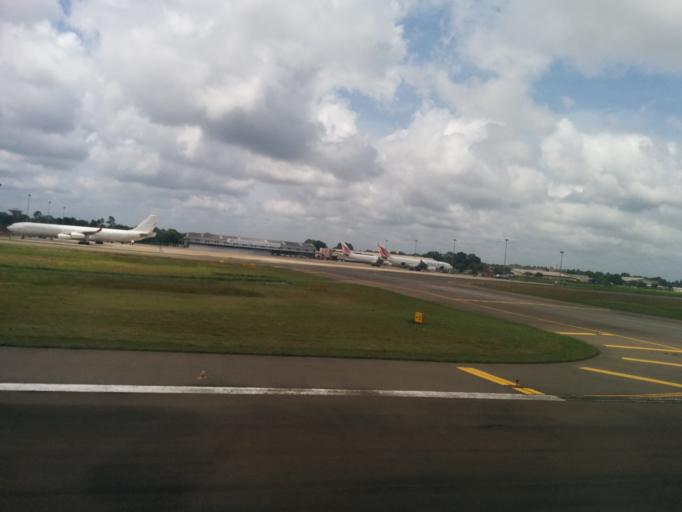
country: LK
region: Western
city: Katunayaka
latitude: 7.1756
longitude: 79.8795
